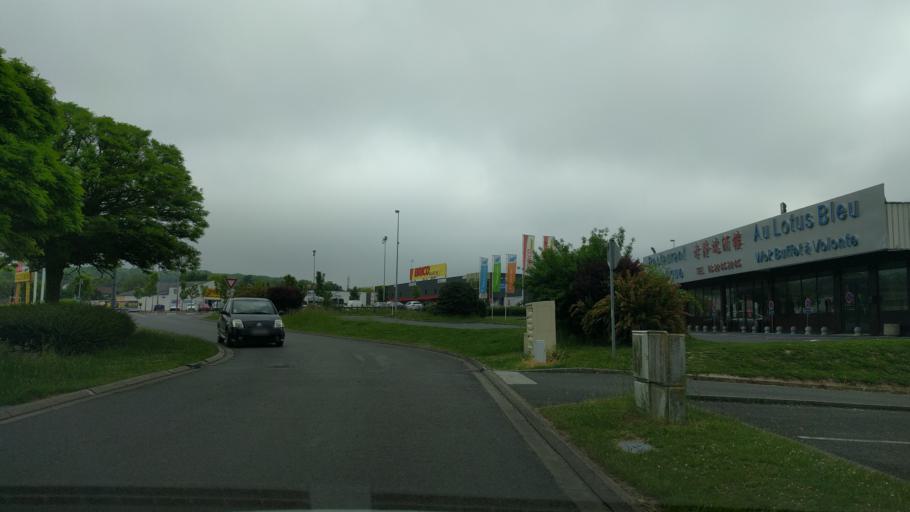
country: FR
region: Picardie
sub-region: Departement de la Somme
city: Peronne
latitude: 49.9410
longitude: 2.9306
